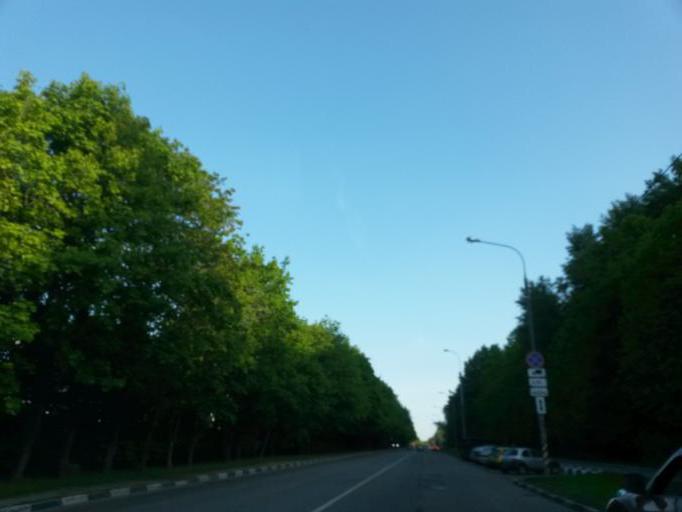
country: RU
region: Moskovskaya
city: Biryulevo Zapadnoye
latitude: 55.5905
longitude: 37.6546
